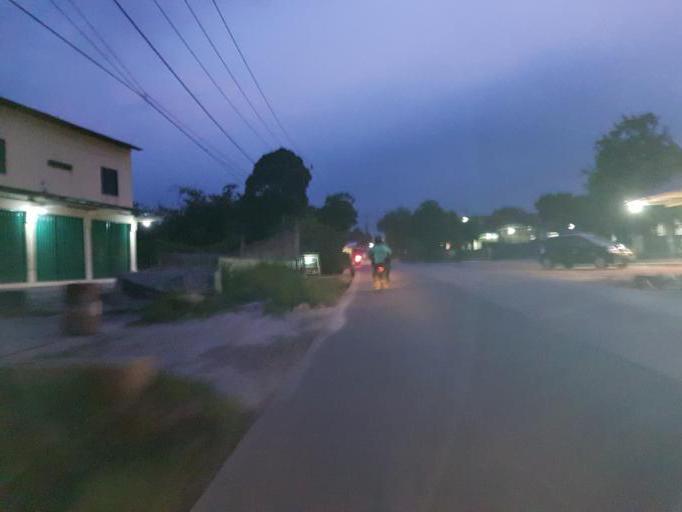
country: ID
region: West Java
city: Serpong
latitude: -6.3120
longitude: 106.6563
